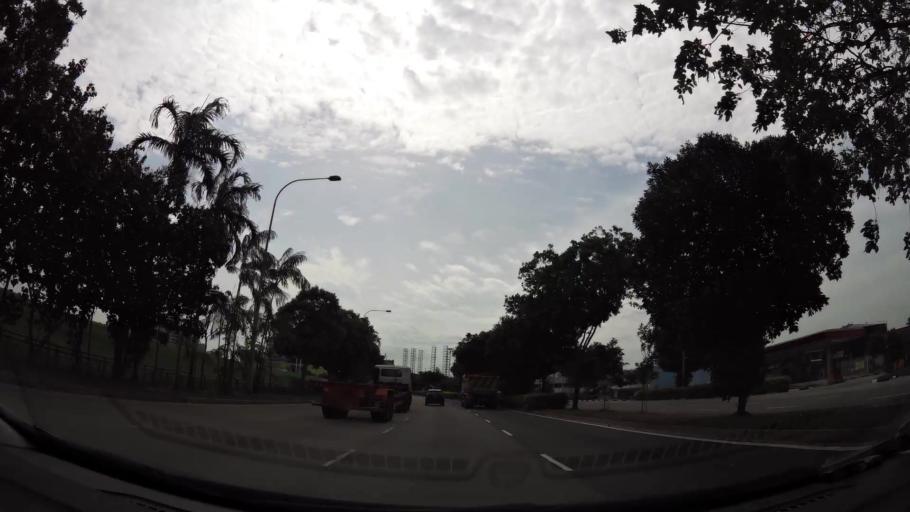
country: SG
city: Singapore
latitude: 1.3052
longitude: 103.7421
